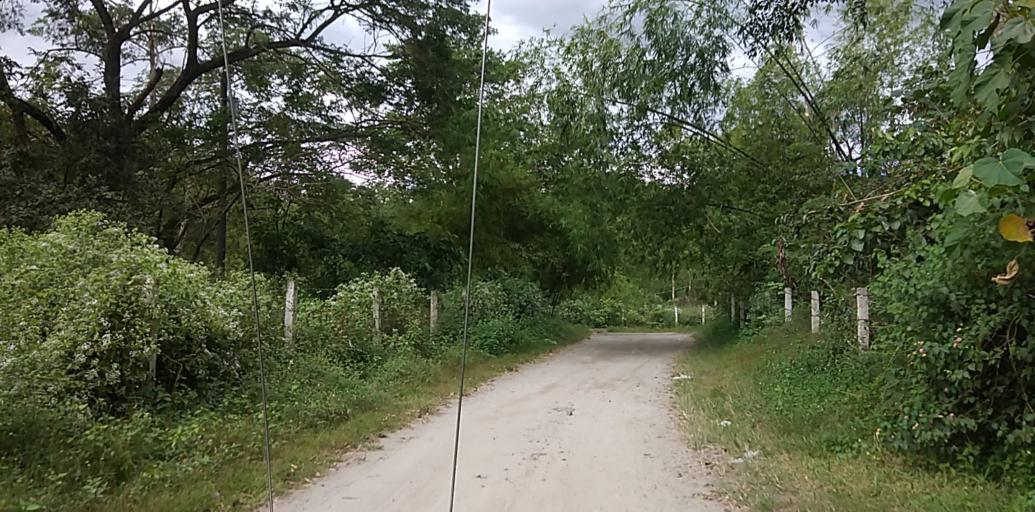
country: PH
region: Central Luzon
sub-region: Province of Pampanga
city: Babo-Pangulo
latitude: 15.1110
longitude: 120.5004
